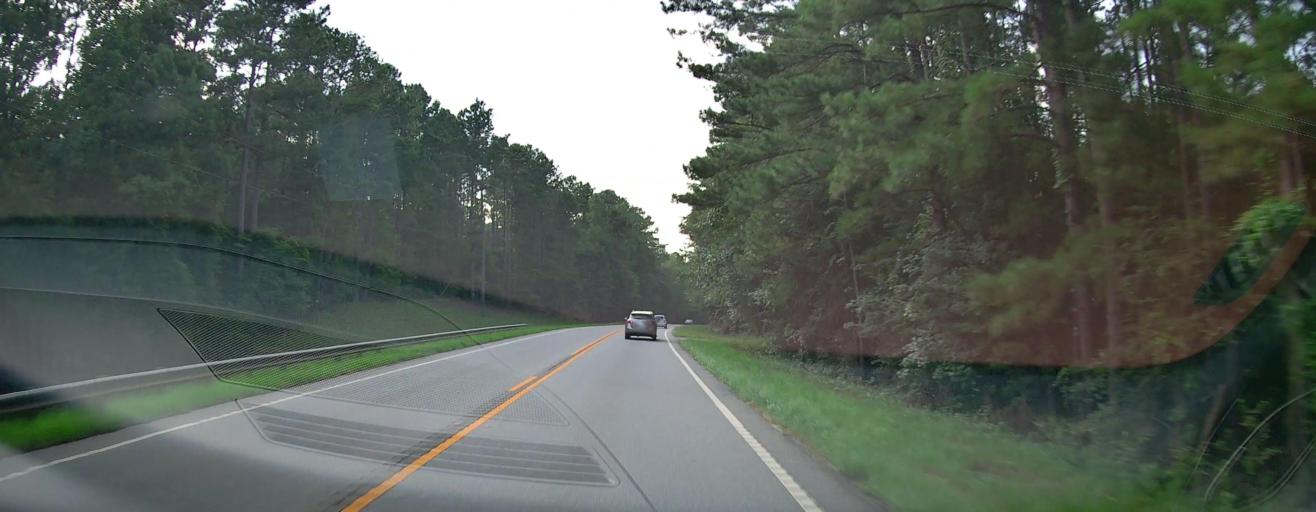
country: US
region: Georgia
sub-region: Monroe County
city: Forsyth
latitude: 33.0387
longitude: -83.7538
